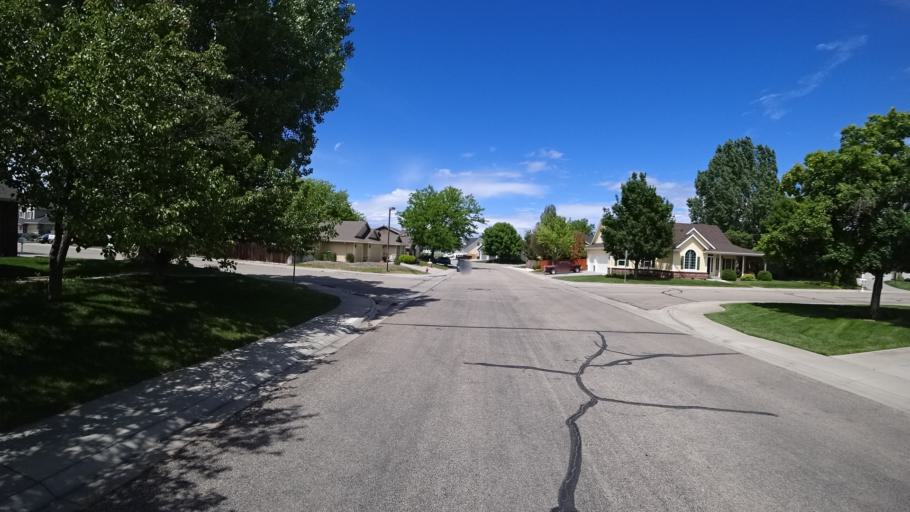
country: US
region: Idaho
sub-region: Ada County
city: Meridian
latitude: 43.5721
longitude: -116.4038
